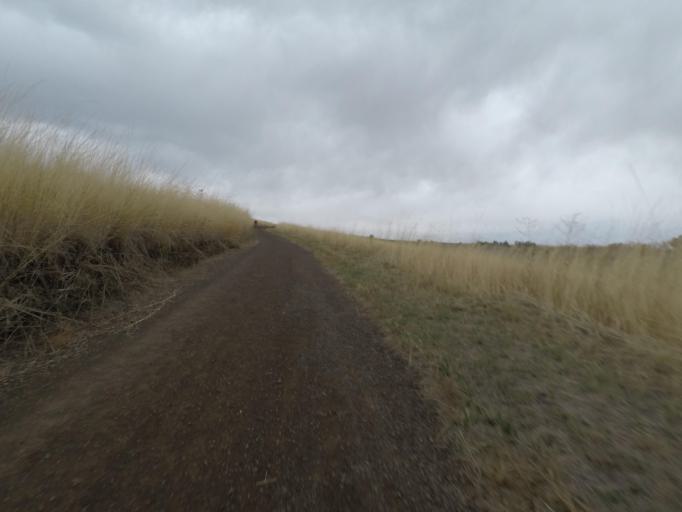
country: US
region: Washington
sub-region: Walla Walla County
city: Walla Walla East
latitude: 46.0599
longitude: -118.2585
